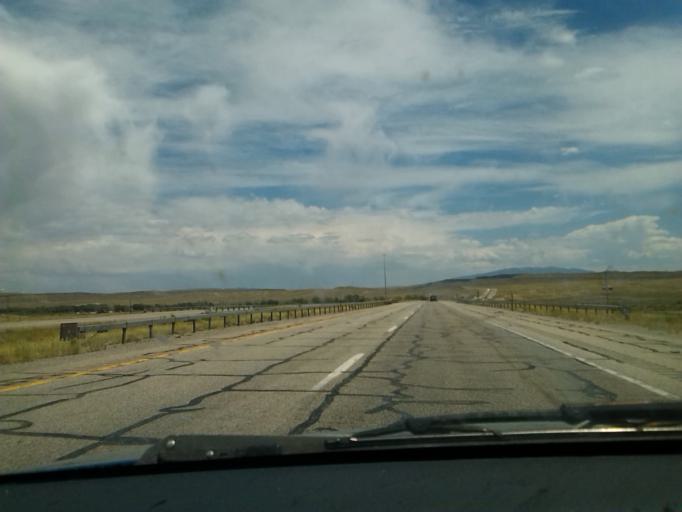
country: US
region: Wyoming
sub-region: Carbon County
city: Rawlins
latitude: 41.7543
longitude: -106.9627
